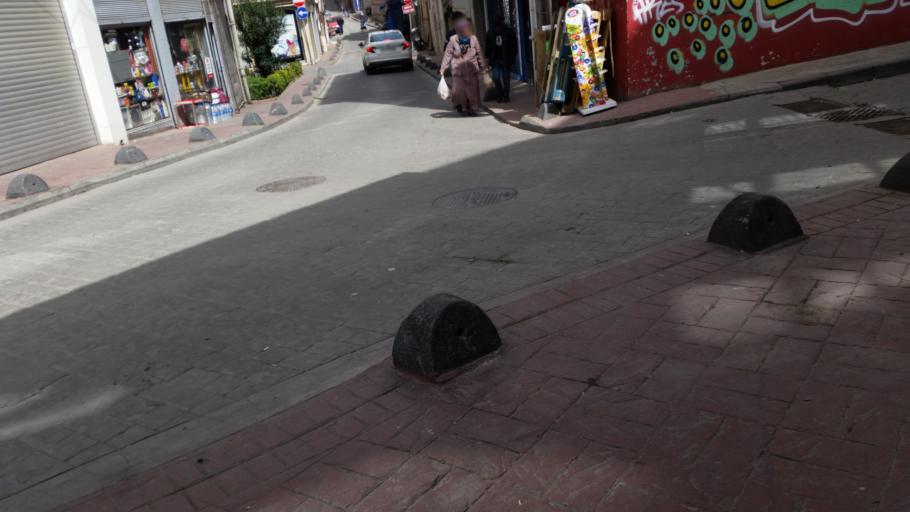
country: TR
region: Istanbul
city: Eminoenue
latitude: 41.0331
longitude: 28.9708
